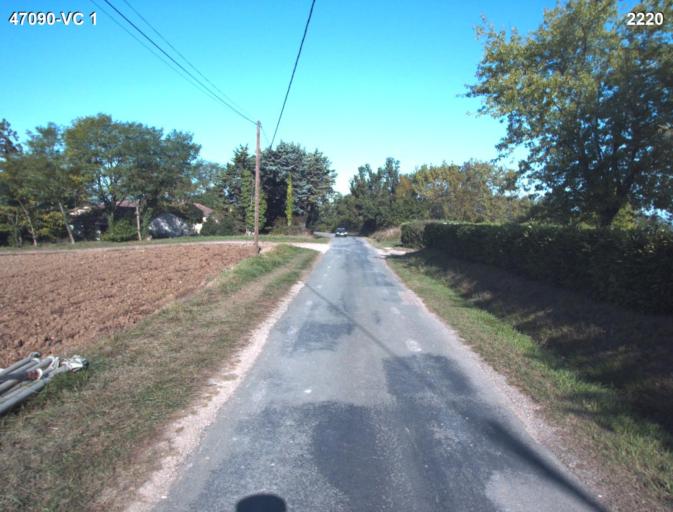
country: FR
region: Aquitaine
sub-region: Departement du Lot-et-Garonne
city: Nerac
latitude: 44.1582
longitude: 0.3921
